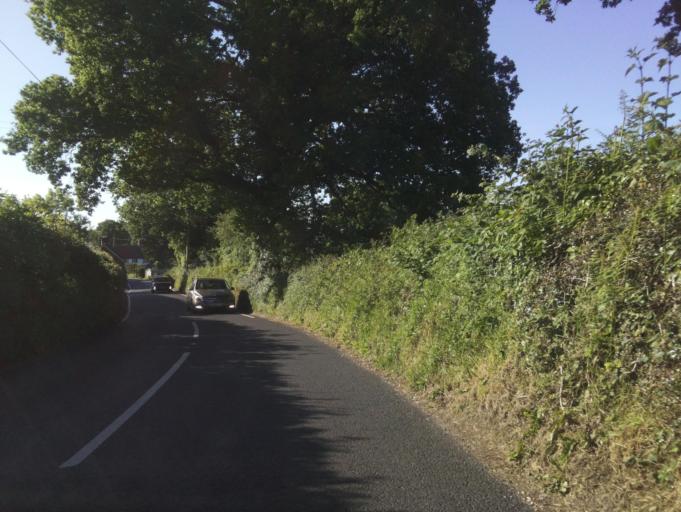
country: GB
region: England
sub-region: Somerset
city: Crewkerne
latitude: 50.8313
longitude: -2.8561
